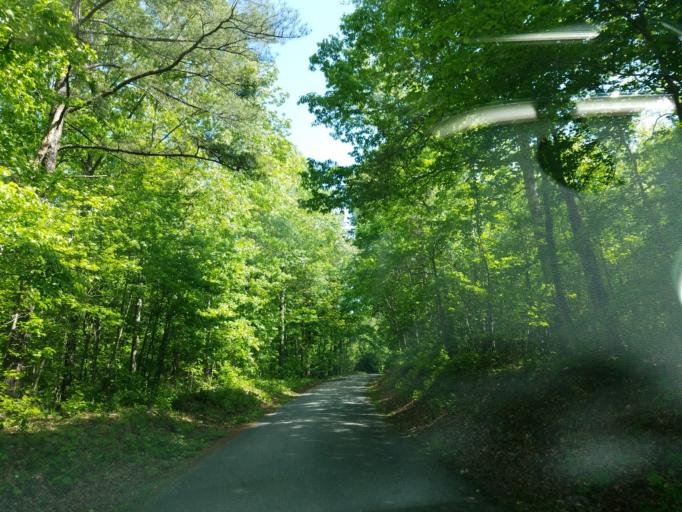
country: US
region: Georgia
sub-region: Cherokee County
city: Ball Ground
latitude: 34.2693
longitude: -84.3127
